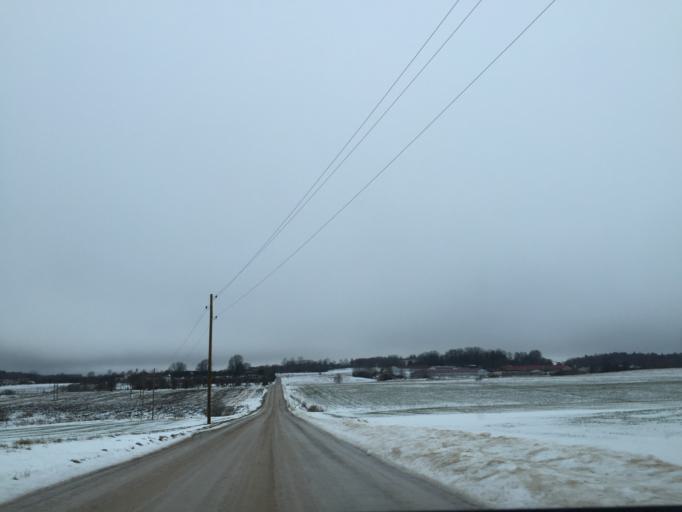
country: LV
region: Krimulda
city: Ragana
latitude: 57.1565
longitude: 24.7205
